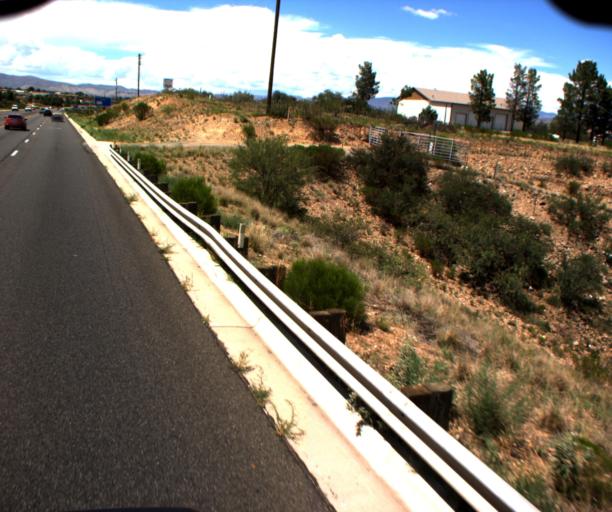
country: US
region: Arizona
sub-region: Yavapai County
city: Verde Village
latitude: 34.7076
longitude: -111.9932
